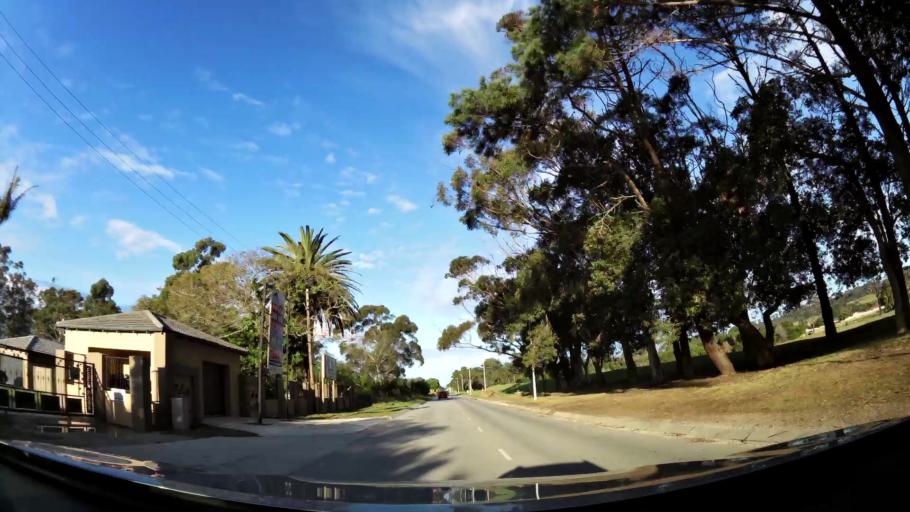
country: ZA
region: Eastern Cape
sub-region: Nelson Mandela Bay Metropolitan Municipality
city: Port Elizabeth
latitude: -33.9755
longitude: 25.5071
